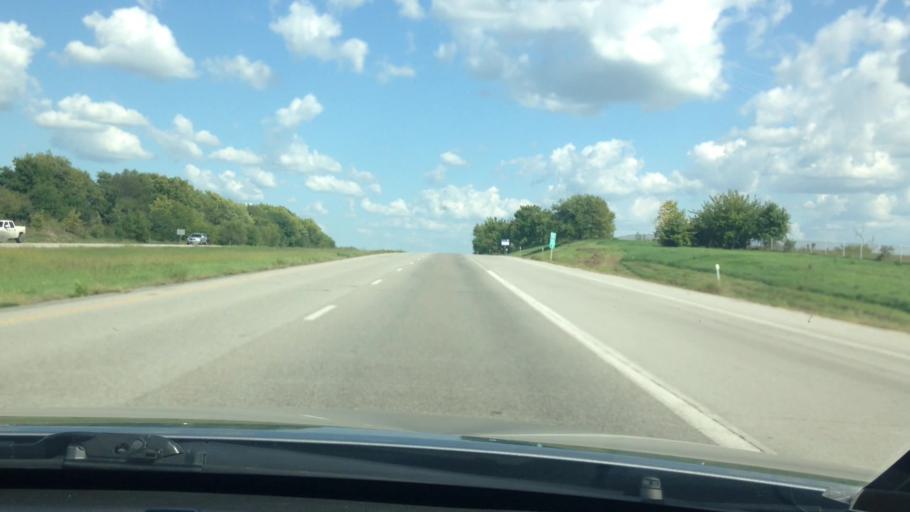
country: US
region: Missouri
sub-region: Clay County
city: Smithville
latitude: 39.3111
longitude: -94.5521
